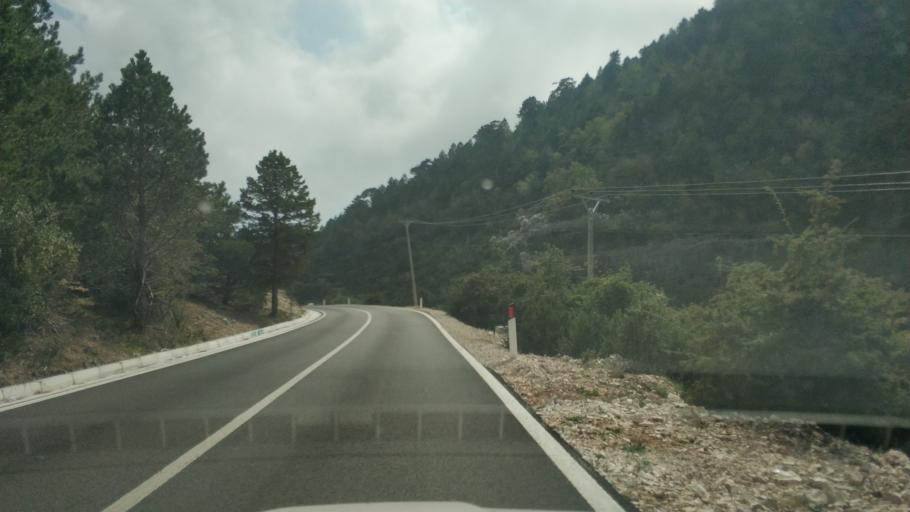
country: AL
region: Vlore
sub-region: Rrethi i Vlores
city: Vranisht
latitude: 40.1999
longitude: 19.5905
